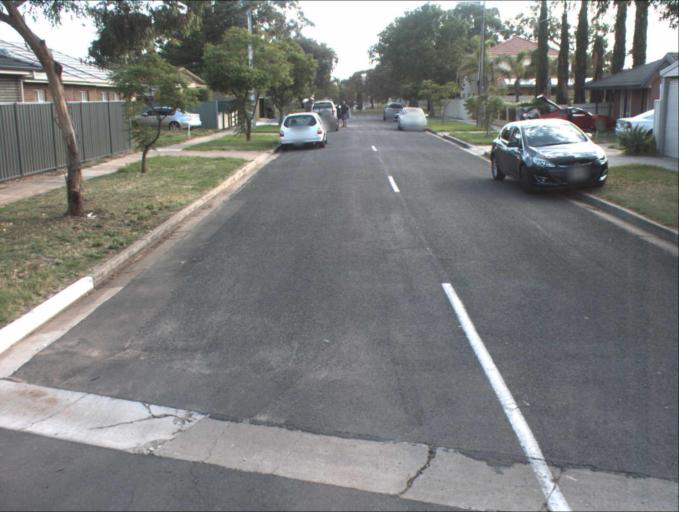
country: AU
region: South Australia
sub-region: Port Adelaide Enfield
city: Klemzig
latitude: -34.8757
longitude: 138.6270
